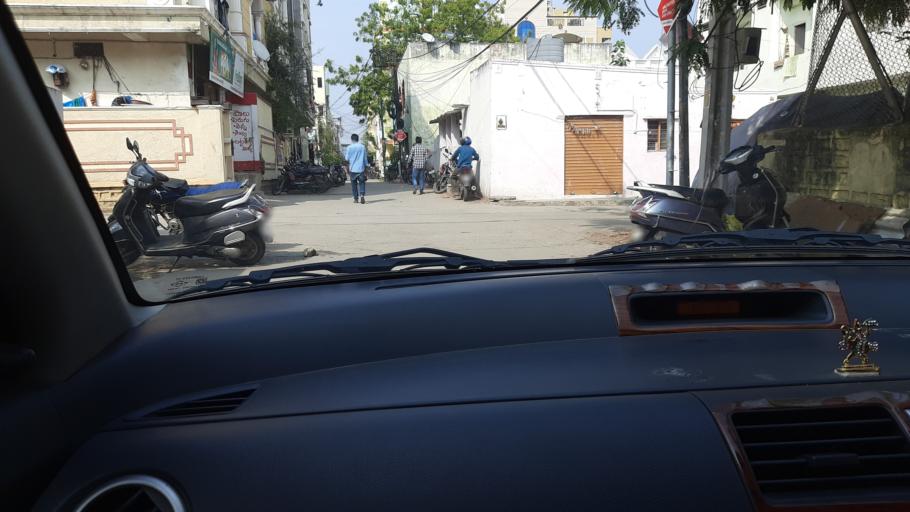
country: IN
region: Telangana
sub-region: Rangareddi
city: Quthbullapur
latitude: 17.4476
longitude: 78.4581
